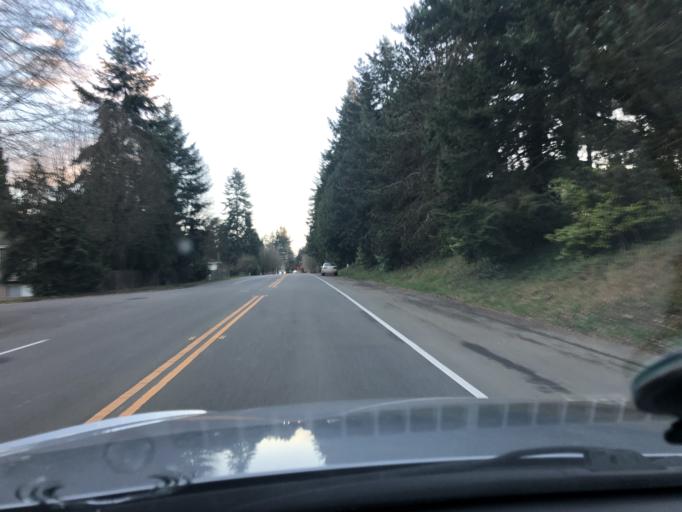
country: US
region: Washington
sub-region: Pierce County
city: Fife Heights
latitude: 47.3185
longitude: -122.3928
